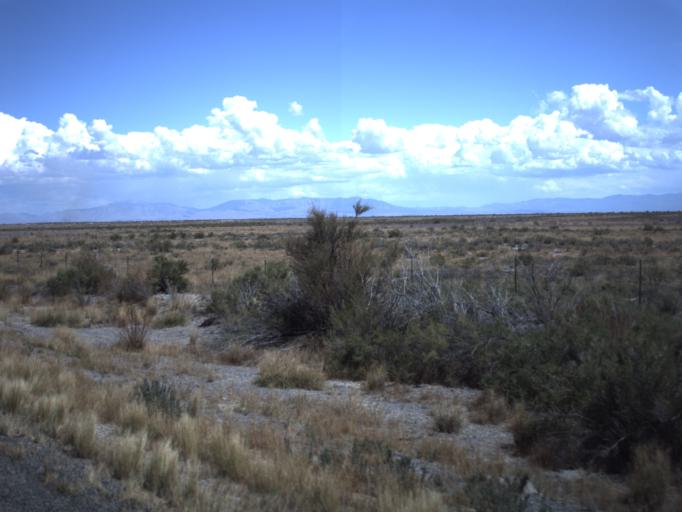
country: US
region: Utah
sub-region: Millard County
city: Delta
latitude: 39.2878
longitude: -112.8329
